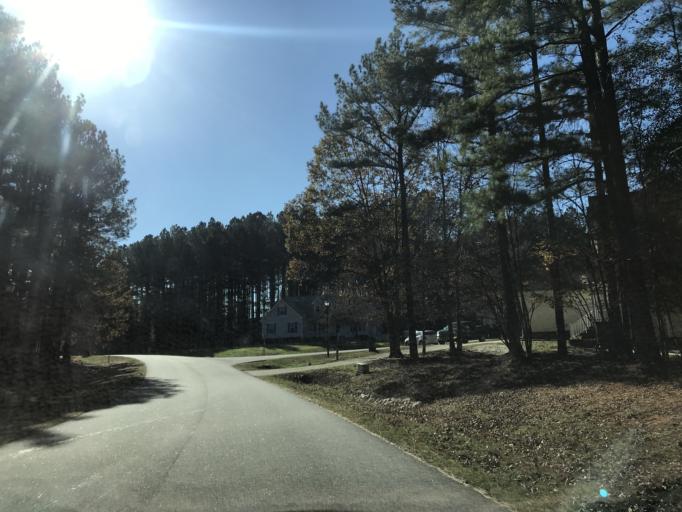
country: US
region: North Carolina
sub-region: Wake County
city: Rolesville
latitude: 35.9680
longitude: -78.3683
